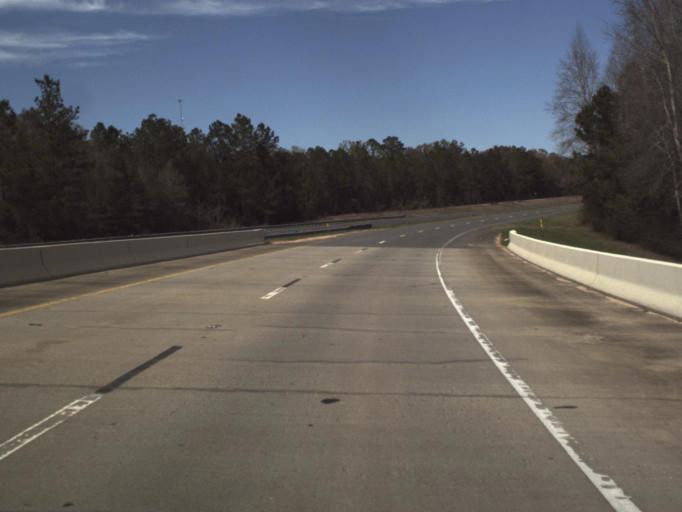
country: US
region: Florida
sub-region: Bay County
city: Youngstown
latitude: 30.5845
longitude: -85.3946
